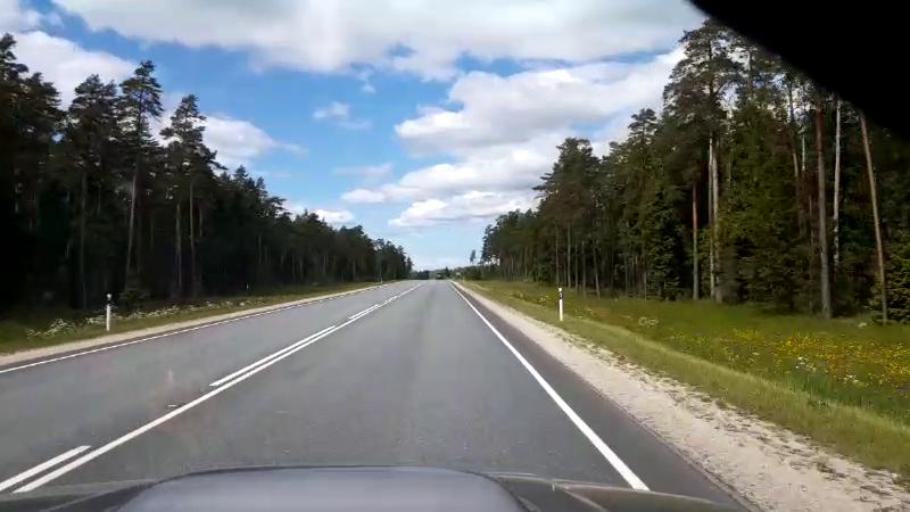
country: EE
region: Raplamaa
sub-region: Maerjamaa vald
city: Marjamaa
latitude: 59.0203
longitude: 24.4511
